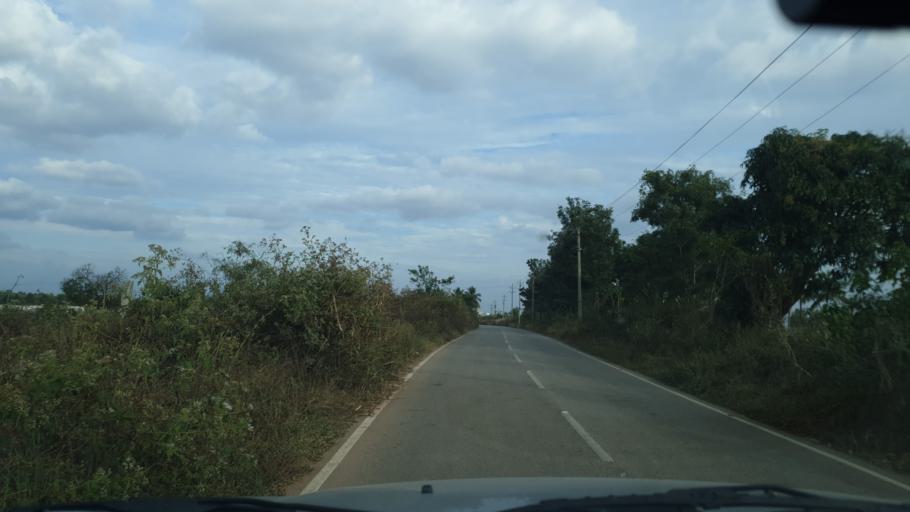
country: IN
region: Karnataka
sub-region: Bangalore Urban
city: Yelahanka
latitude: 13.1999
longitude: 77.6115
